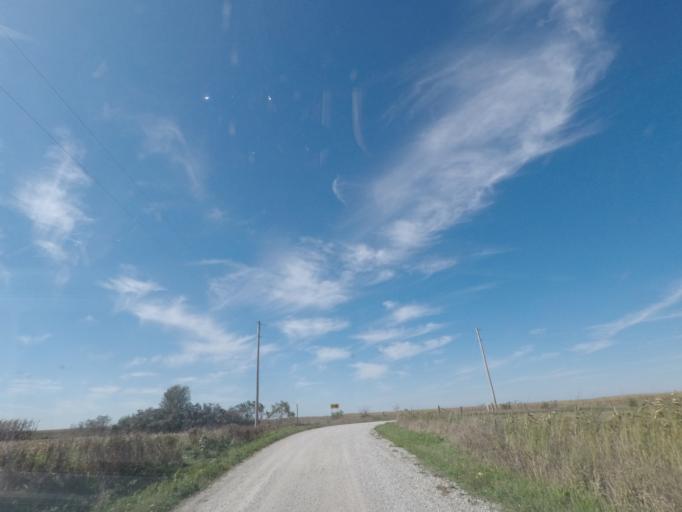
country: US
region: Iowa
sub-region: Story County
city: Nevada
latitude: 42.0126
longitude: -93.3567
